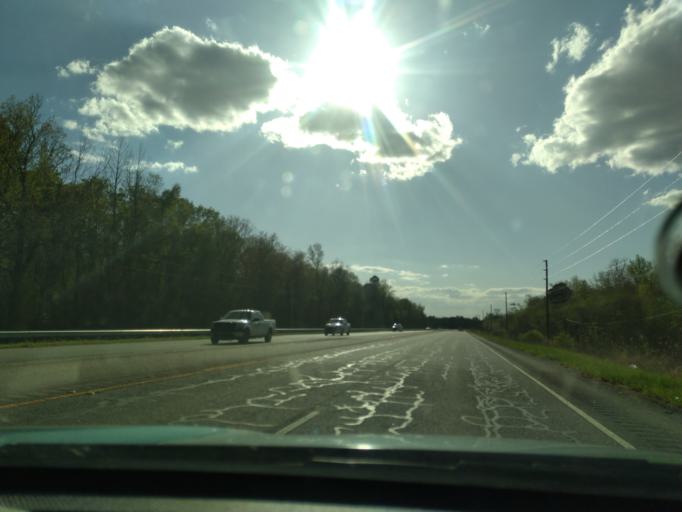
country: US
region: South Carolina
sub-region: Williamsburg County
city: Kingstree
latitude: 33.6578
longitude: -79.8657
